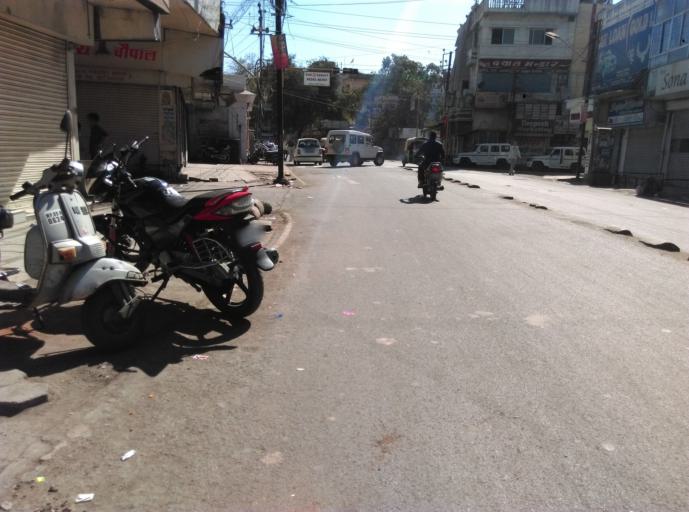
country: IN
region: Madhya Pradesh
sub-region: Indore
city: Indore
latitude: 22.7194
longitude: 75.8628
